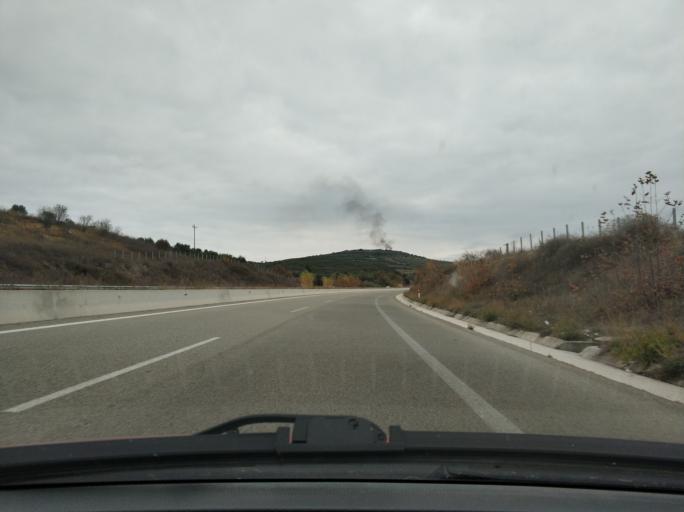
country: GR
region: East Macedonia and Thrace
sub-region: Nomos Kavalas
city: Paralia Ofryniou
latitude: 40.7935
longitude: 23.9795
